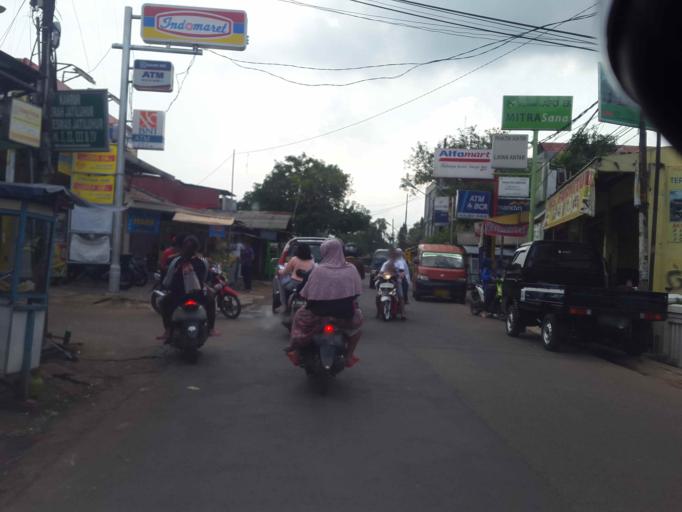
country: ID
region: West Java
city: Cileungsir
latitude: -6.3197
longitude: 106.9488
